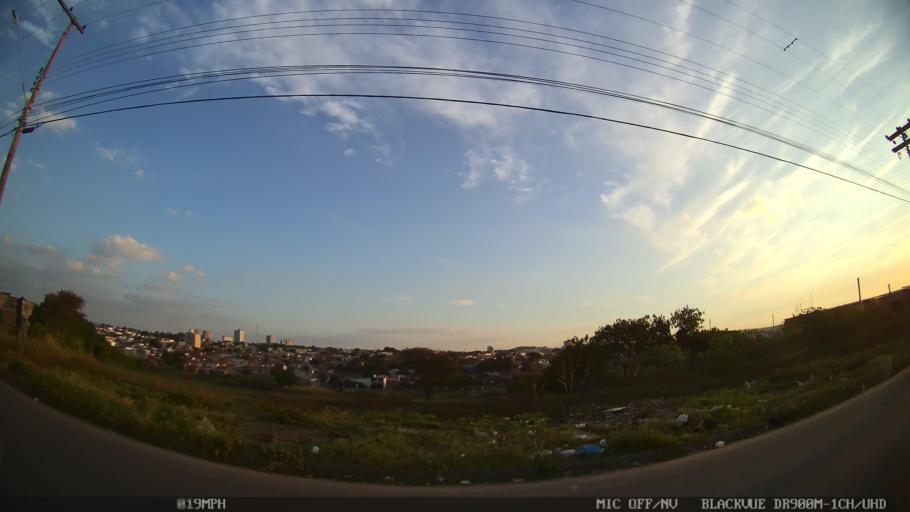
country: BR
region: Sao Paulo
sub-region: Hortolandia
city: Hortolandia
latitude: -22.8628
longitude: -47.2062
